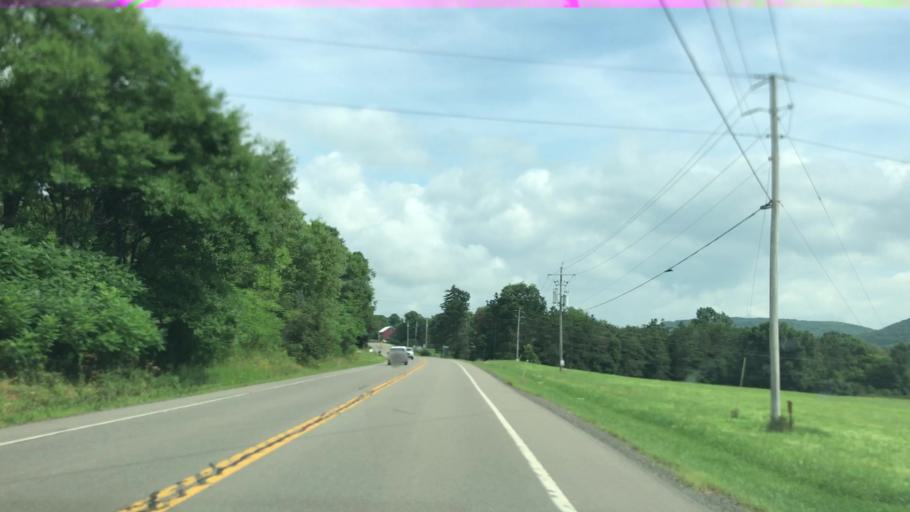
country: US
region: New York
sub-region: Ontario County
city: Naples
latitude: 42.4989
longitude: -77.2864
